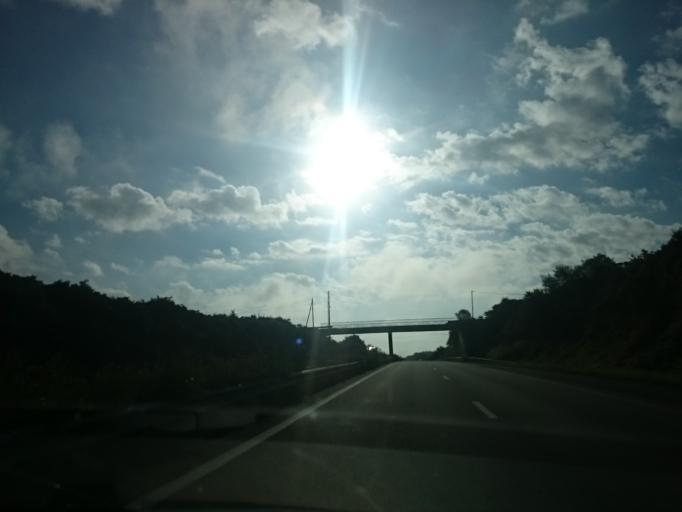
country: FR
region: Brittany
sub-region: Departement du Finistere
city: Guerlesquin
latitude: 48.5681
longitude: -3.5899
